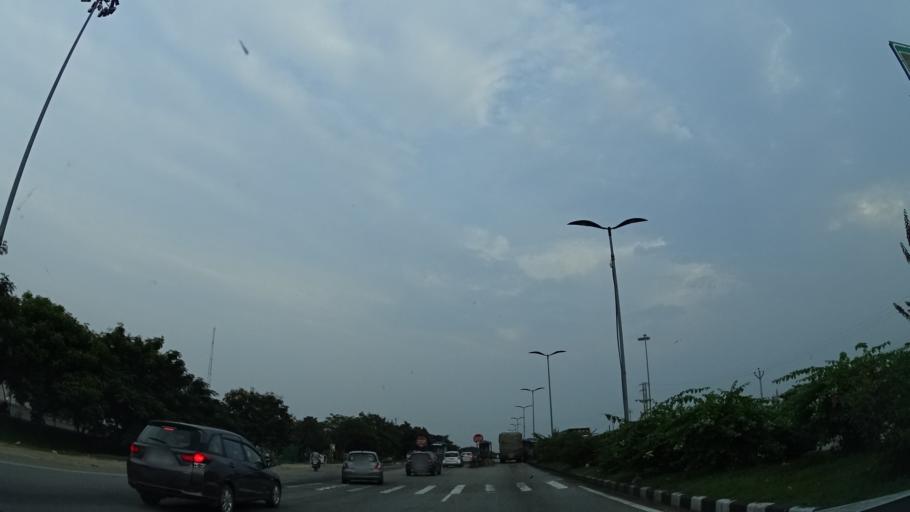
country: IN
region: Telangana
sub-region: Medak
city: Narsingi
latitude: 17.8017
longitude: 78.4717
